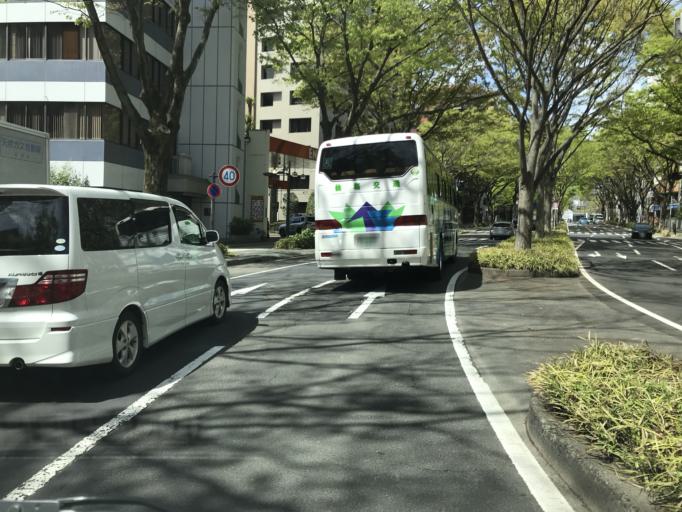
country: JP
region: Miyagi
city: Sendai
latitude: 38.2587
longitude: 140.8674
